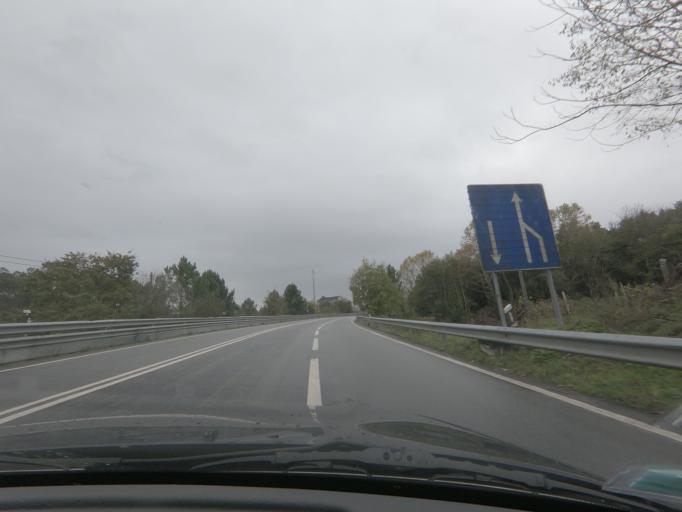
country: PT
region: Porto
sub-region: Amarante
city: Amarante
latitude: 41.3065
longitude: -8.0751
